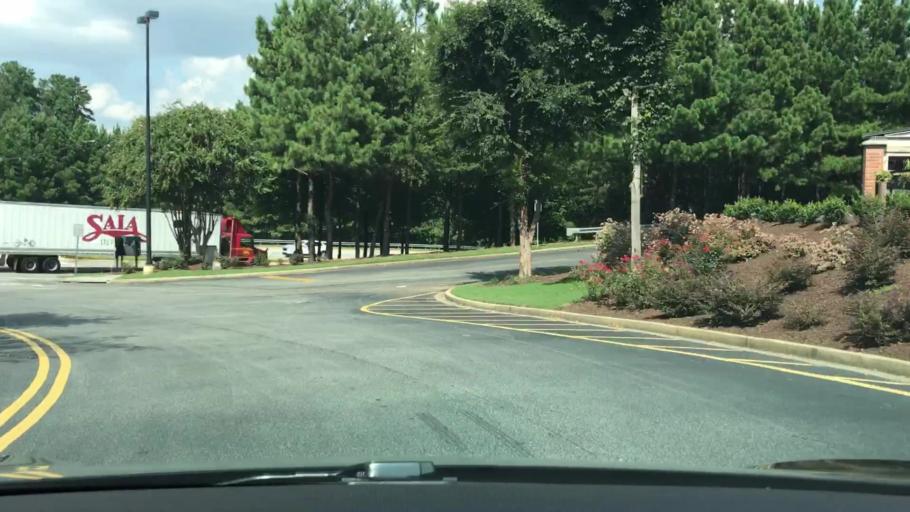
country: US
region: Georgia
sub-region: Gwinnett County
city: Suwanee
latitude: 34.0386
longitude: -84.0484
